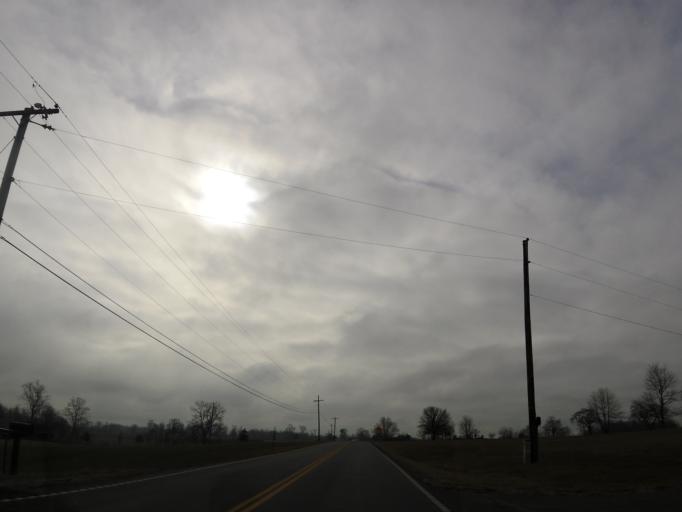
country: US
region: Kentucky
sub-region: Trimble County
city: Bedford
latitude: 38.6513
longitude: -85.3231
